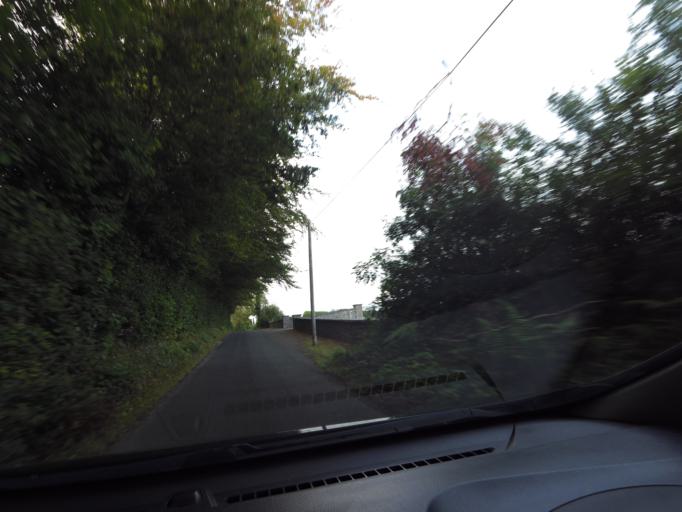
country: IE
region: Connaught
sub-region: County Galway
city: Ballinasloe
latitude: 53.3044
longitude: -8.1009
